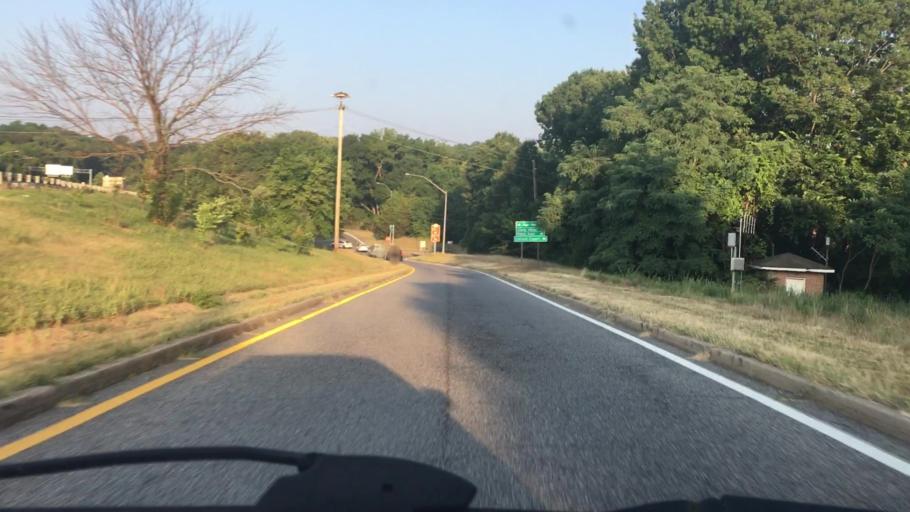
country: US
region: Maryland
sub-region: Prince George's County
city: Upper Marlboro
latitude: 38.8136
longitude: -76.7482
